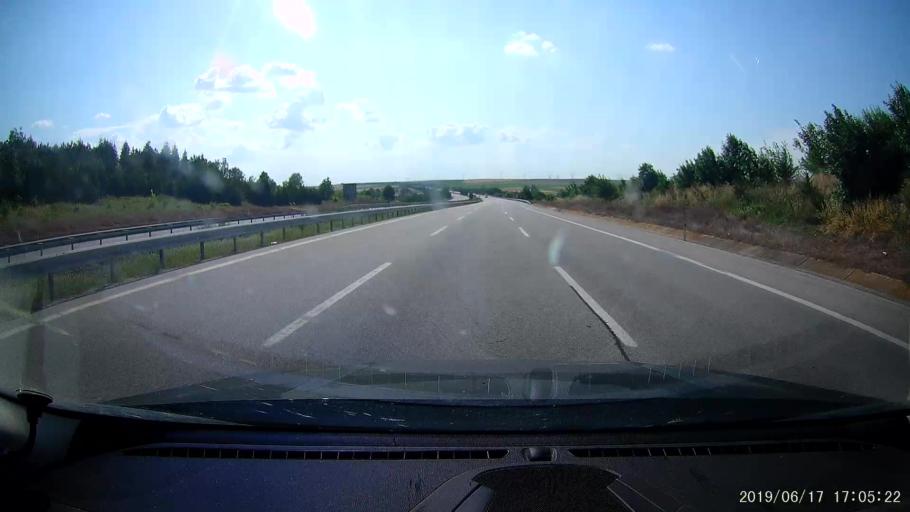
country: TR
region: Edirne
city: Edirne
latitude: 41.6592
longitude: 26.7014
